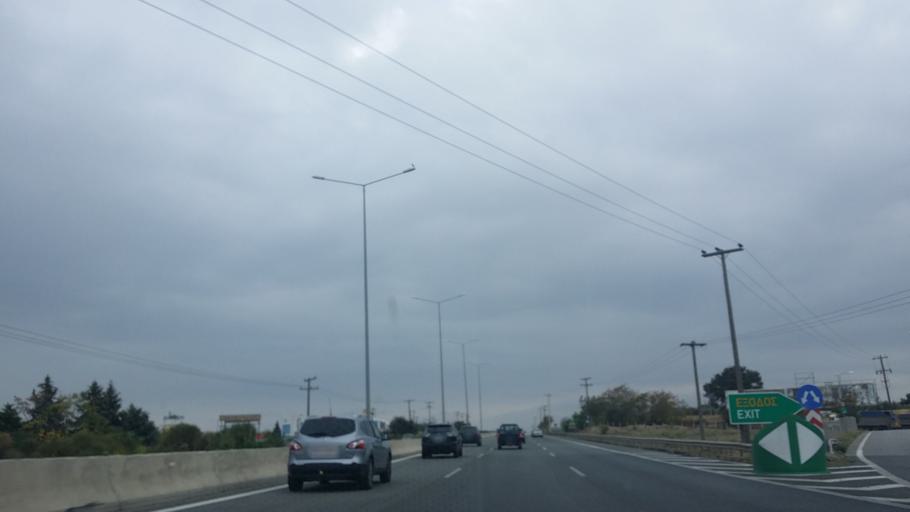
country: GR
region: Central Greece
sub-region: Nomos Voiotias
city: Oinofyta
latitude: 38.3270
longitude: 23.6092
